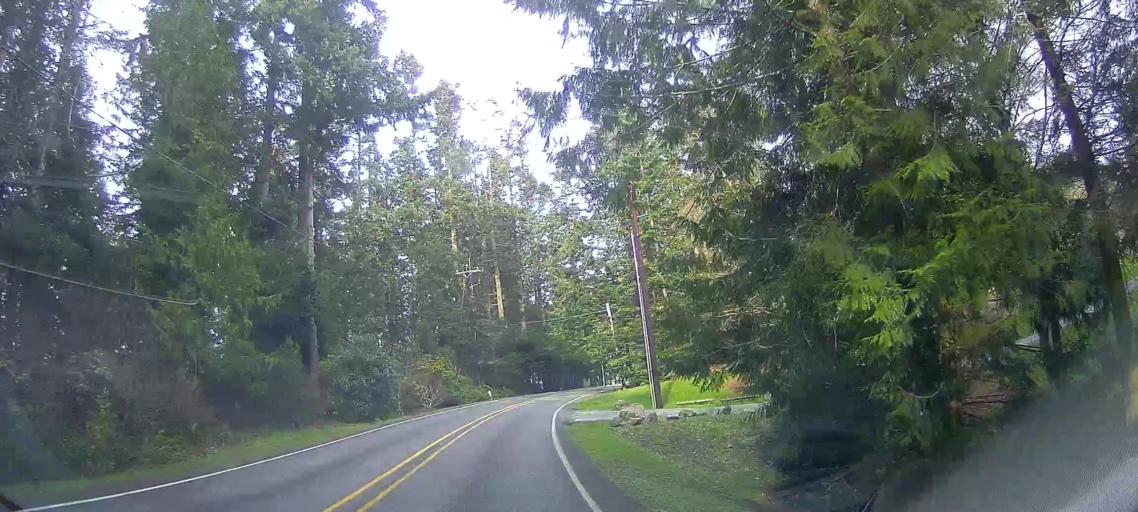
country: US
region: Washington
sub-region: Island County
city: Camano
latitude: 48.2426
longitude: -122.5313
